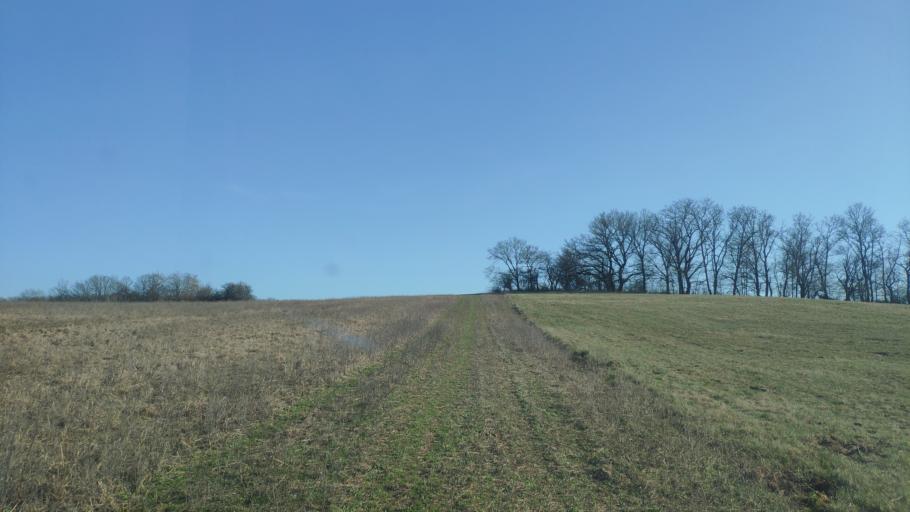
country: SK
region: Banskobystricky
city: Revuca
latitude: 48.5448
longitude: 20.2561
